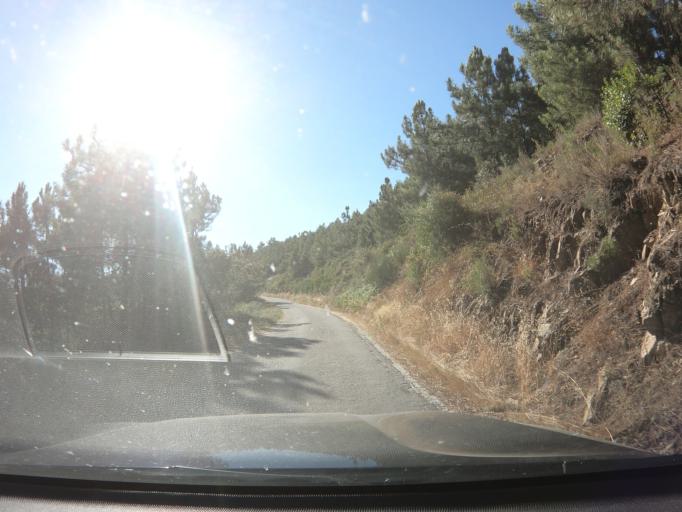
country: PT
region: Vila Real
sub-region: Sabrosa
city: Vilela
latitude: 41.2244
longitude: -7.5846
